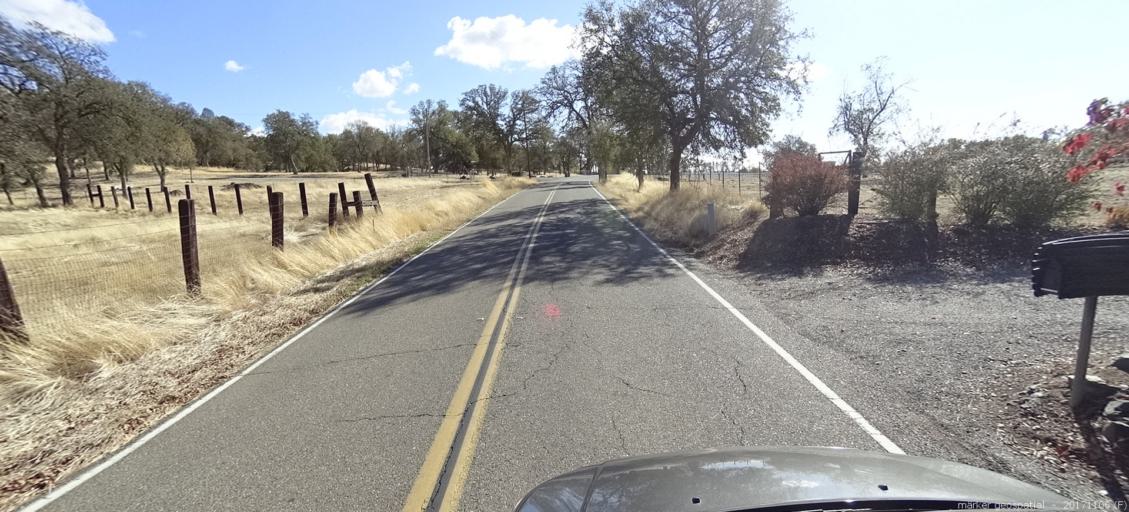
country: US
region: California
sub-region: Shasta County
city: Palo Cedro
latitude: 40.5801
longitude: -122.2205
